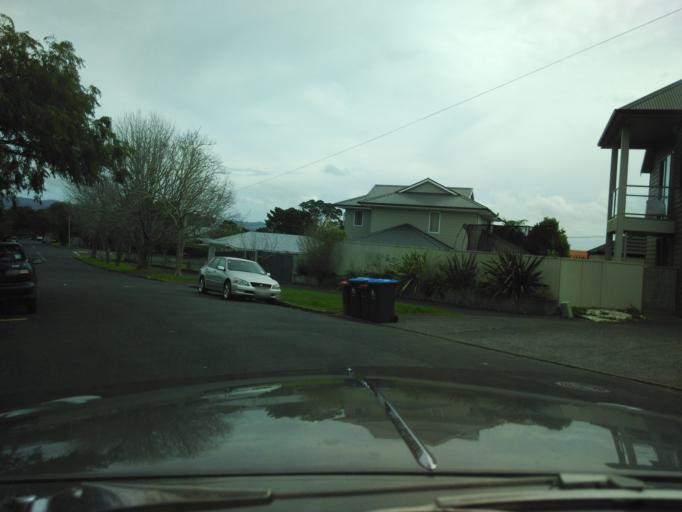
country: NZ
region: Auckland
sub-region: Auckland
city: Rosebank
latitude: -36.8594
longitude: 174.7019
